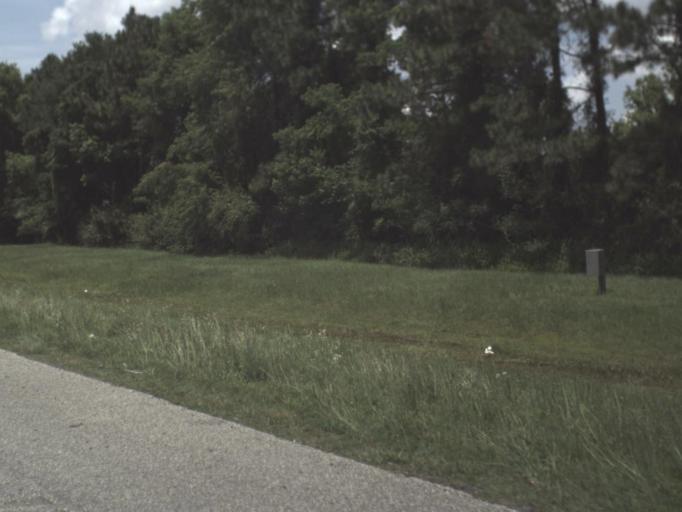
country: US
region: Florida
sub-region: Saint Johns County
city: Fruit Cove
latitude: 30.1734
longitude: -81.6156
